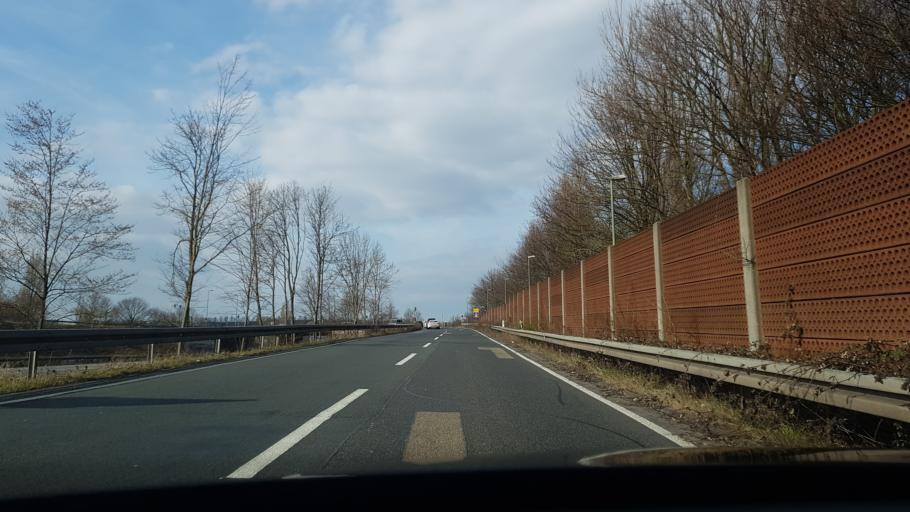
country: DE
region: North Rhine-Westphalia
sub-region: Regierungsbezirk Dusseldorf
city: Dinslaken
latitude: 51.5258
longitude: 6.7590
